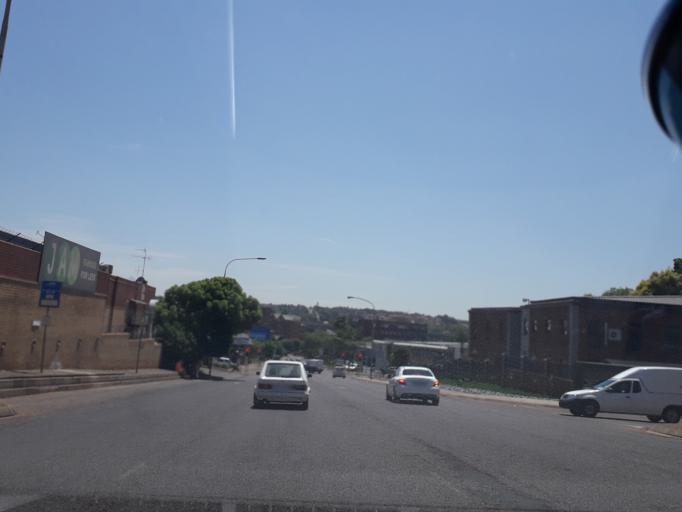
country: ZA
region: Gauteng
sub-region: City of Tshwane Metropolitan Municipality
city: Centurion
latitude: -25.8602
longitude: 28.1877
